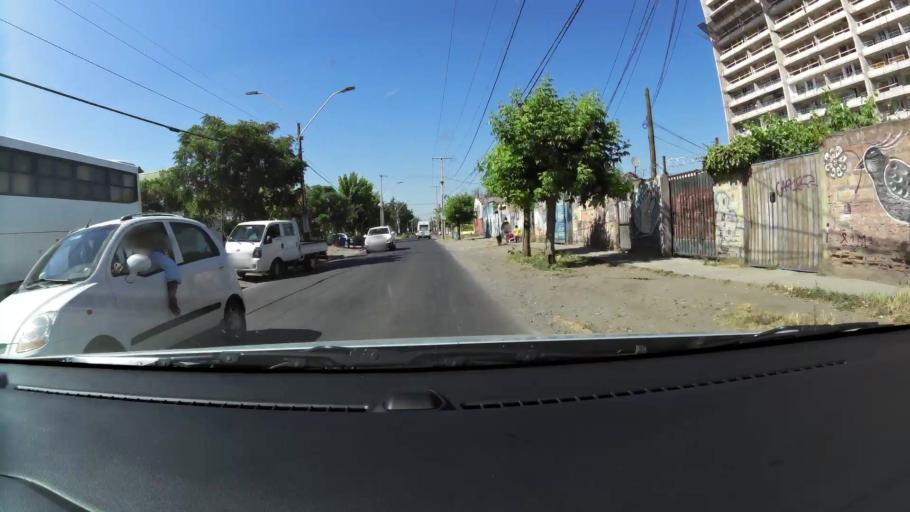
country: CL
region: Santiago Metropolitan
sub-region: Provincia de Santiago
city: La Pintana
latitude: -33.5422
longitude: -70.6514
